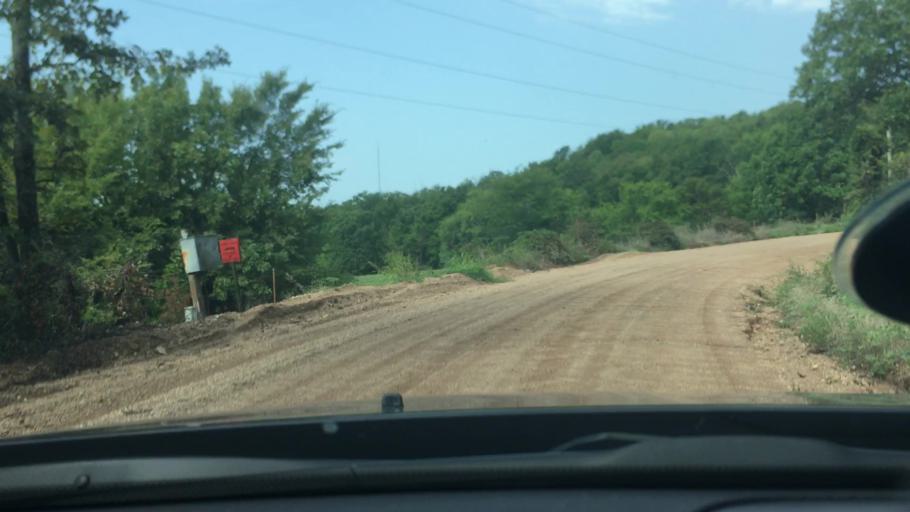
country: US
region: Oklahoma
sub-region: Atoka County
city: Atoka
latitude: 34.4393
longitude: -96.0627
